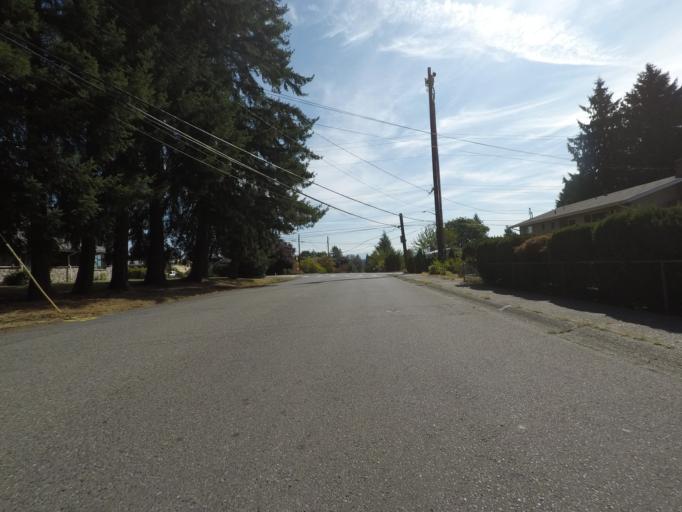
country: US
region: Washington
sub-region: King County
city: Inglewood-Finn Hill
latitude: 47.7333
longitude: -122.2298
